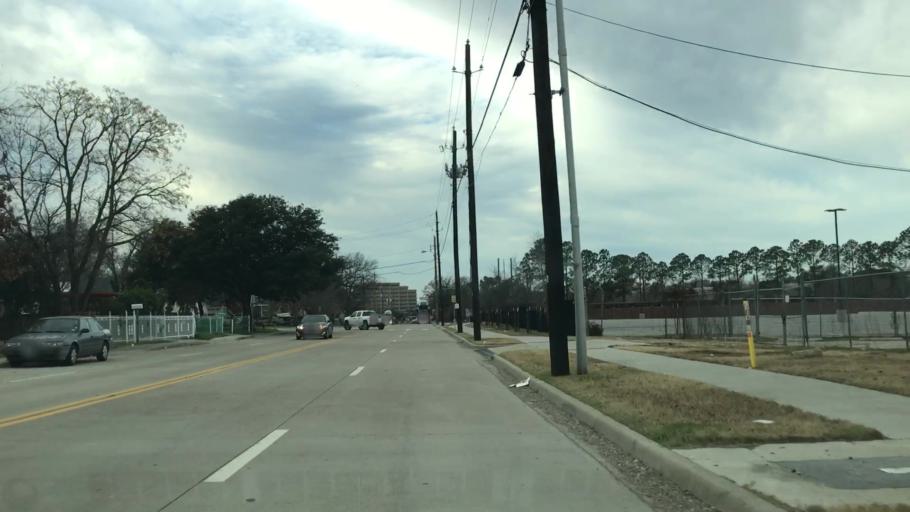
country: US
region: Texas
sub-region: Dallas County
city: University Park
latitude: 32.8403
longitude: -96.8618
